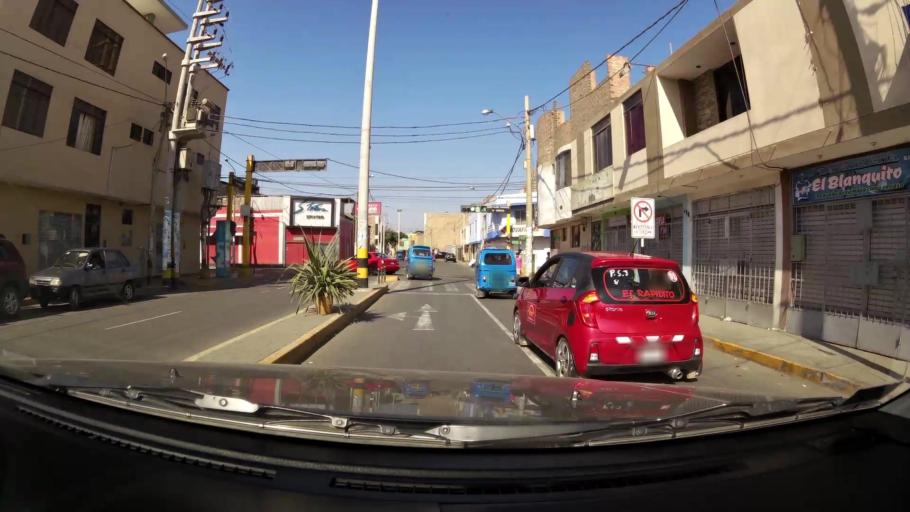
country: PE
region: Ica
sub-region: Provincia de Chincha
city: Chincha Alta
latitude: -13.4212
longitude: -76.1333
